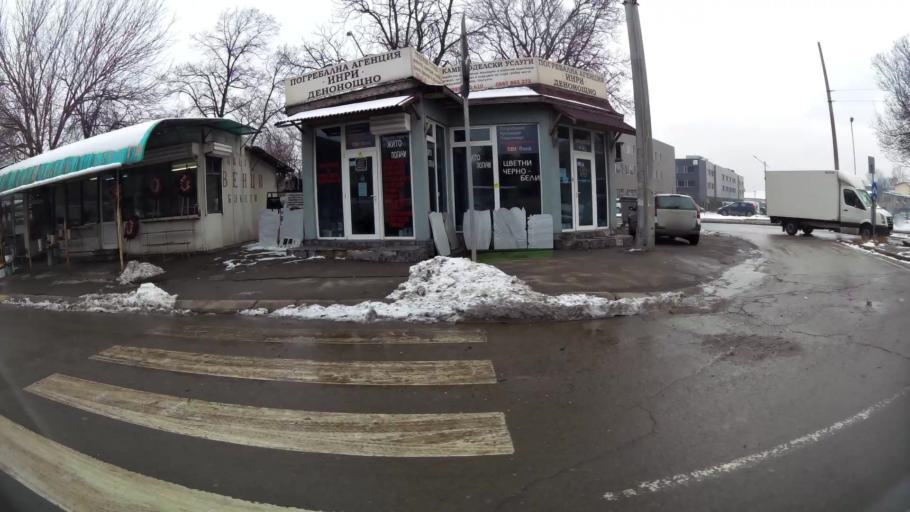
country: BG
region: Sofia-Capital
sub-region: Stolichna Obshtina
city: Sofia
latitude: 42.7113
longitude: 23.3370
